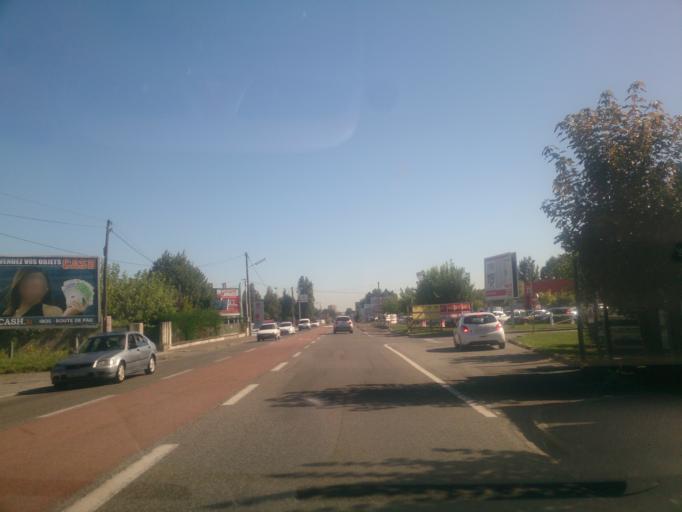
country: FR
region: Midi-Pyrenees
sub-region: Departement des Hautes-Pyrenees
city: Odos
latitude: 43.2127
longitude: 0.0505
